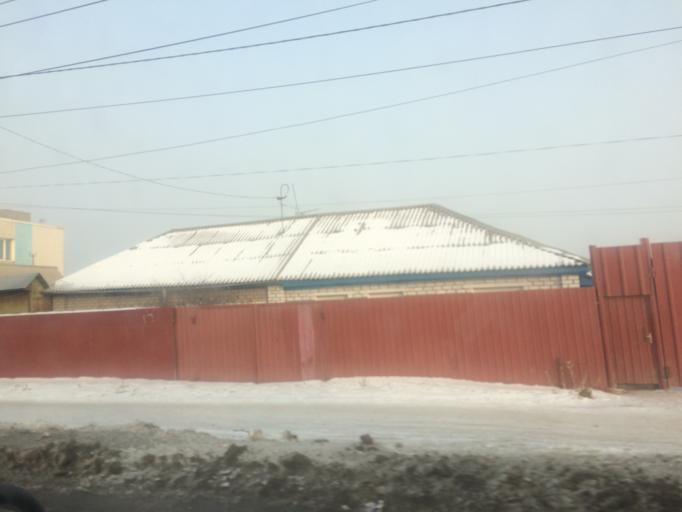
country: RU
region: Chelyabinsk
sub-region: Gorod Magnitogorsk
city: Magnitogorsk
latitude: 53.4275
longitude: 58.9618
